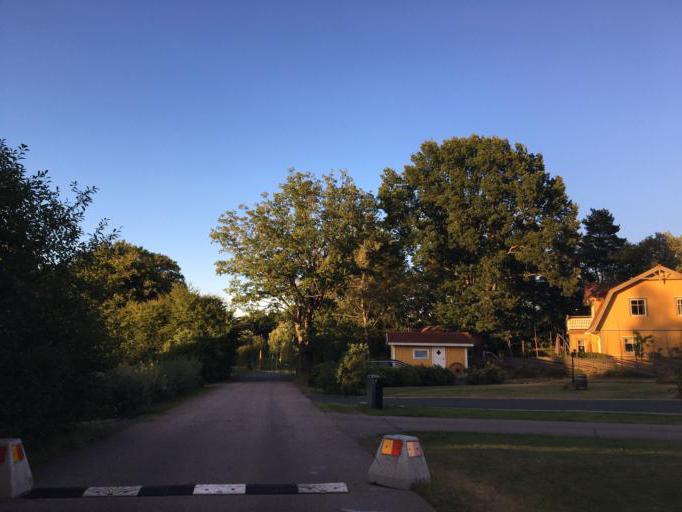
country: SE
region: Soedermanland
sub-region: Eskilstuna Kommun
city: Torshalla
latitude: 59.4350
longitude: 16.4583
